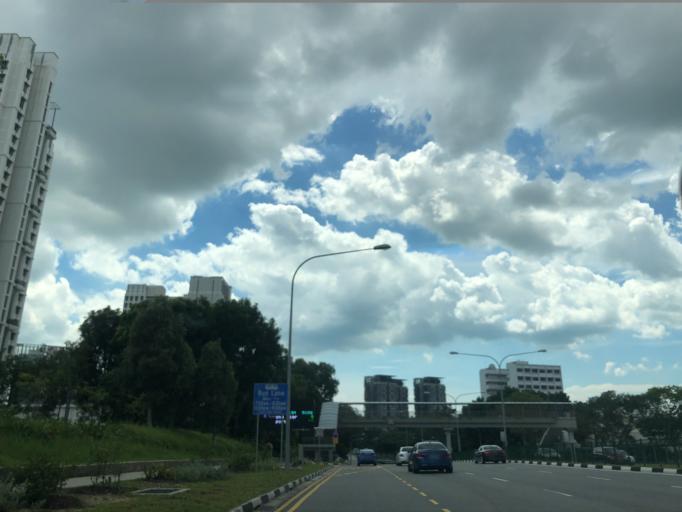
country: SG
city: Singapore
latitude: 1.3095
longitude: 103.7718
